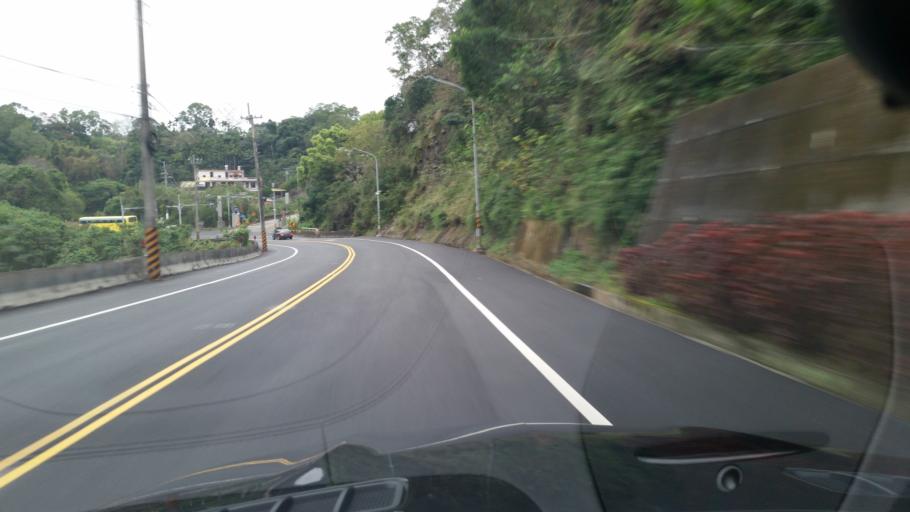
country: TW
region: Taiwan
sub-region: Miaoli
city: Miaoli
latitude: 24.5821
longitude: 120.8763
